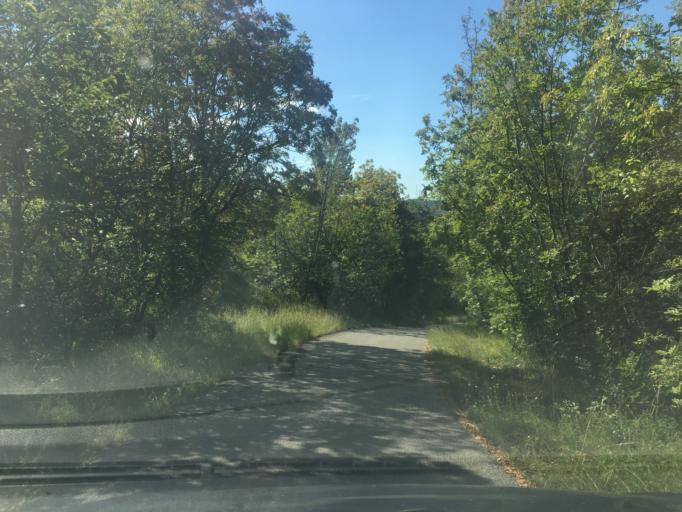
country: IT
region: Friuli Venezia Giulia
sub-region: Provincia di Trieste
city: Zolla
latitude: 45.7154
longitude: 13.8012
